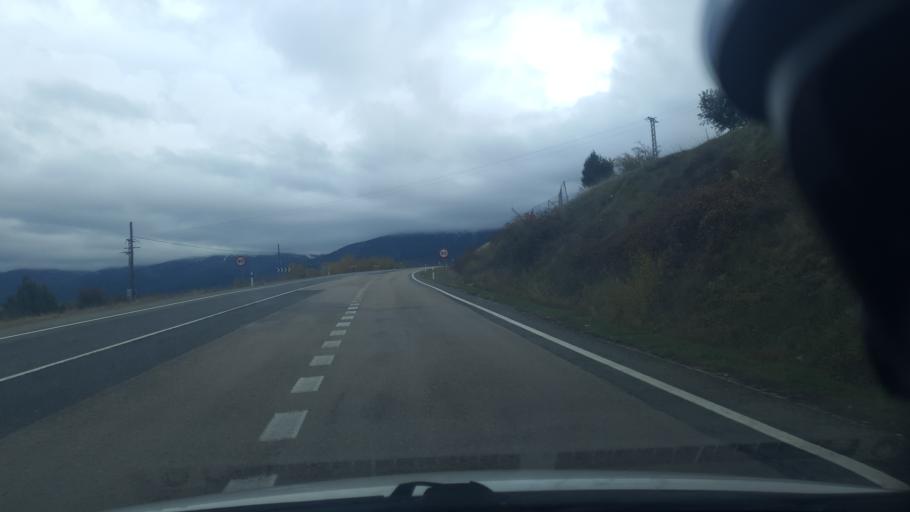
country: ES
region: Castille and Leon
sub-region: Provincia de Segovia
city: Cerezo de Abajo
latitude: 41.2156
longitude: -3.5882
